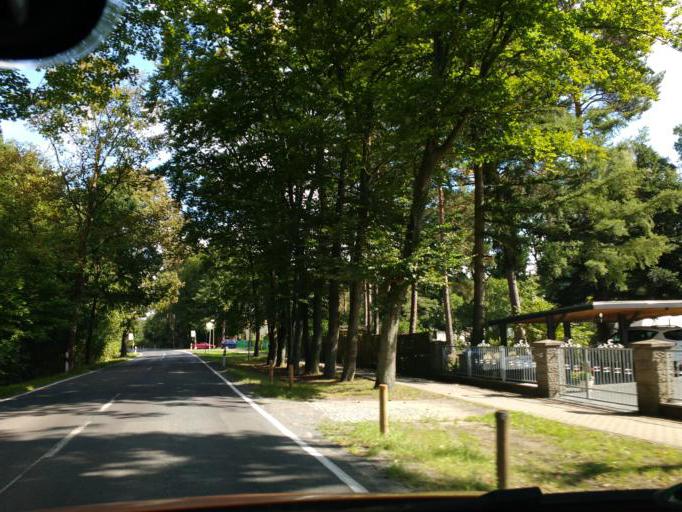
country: DE
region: Brandenburg
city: Wandlitz
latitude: 52.7226
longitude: 13.3722
